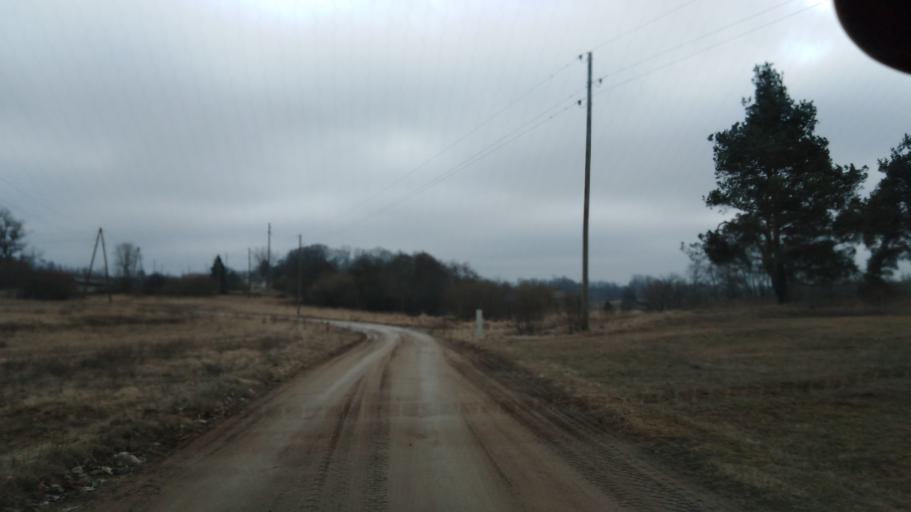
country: LV
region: Kuldigas Rajons
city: Kuldiga
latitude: 56.9842
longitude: 21.9670
